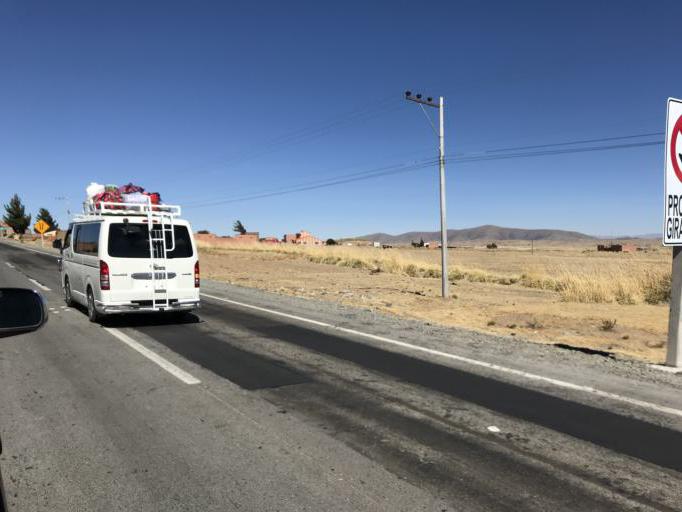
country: BO
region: La Paz
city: Batallas
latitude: -16.2552
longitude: -68.5653
